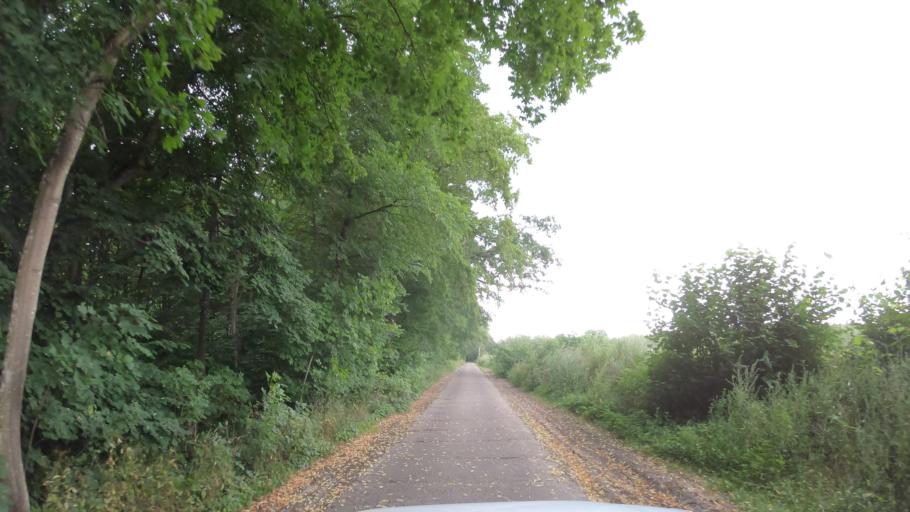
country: PL
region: West Pomeranian Voivodeship
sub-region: Powiat stargardzki
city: Dolice
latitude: 53.1914
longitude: 15.2916
